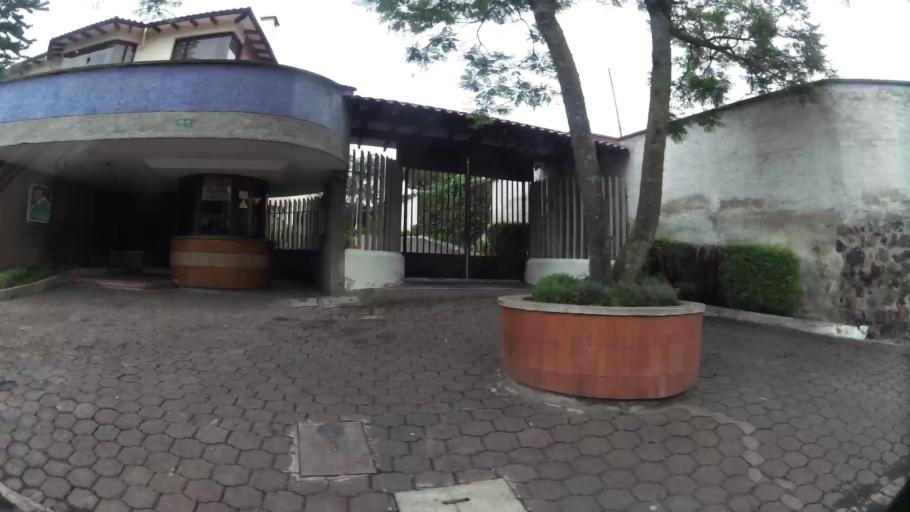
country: EC
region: Pichincha
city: Sangolqui
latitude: -0.3029
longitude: -78.4630
